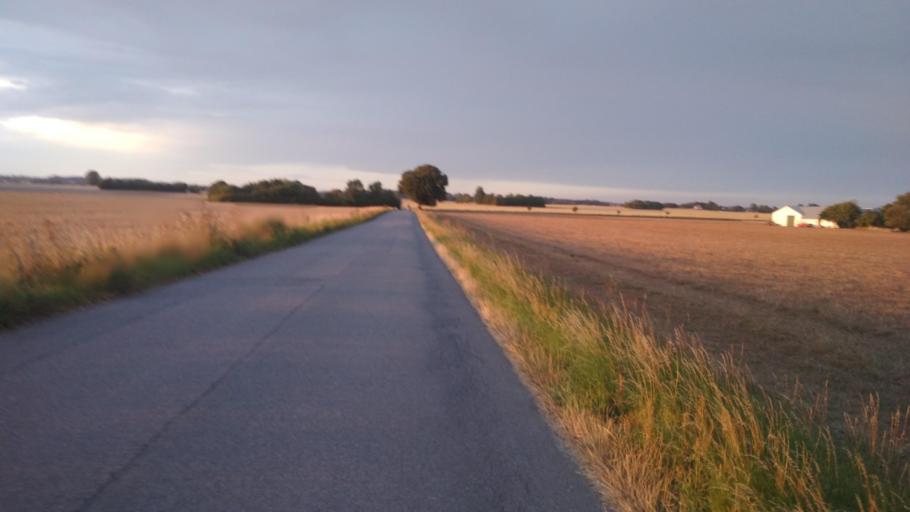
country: DK
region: Capital Region
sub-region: Bornholm Kommune
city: Akirkeby
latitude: 55.0311
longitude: 14.9132
